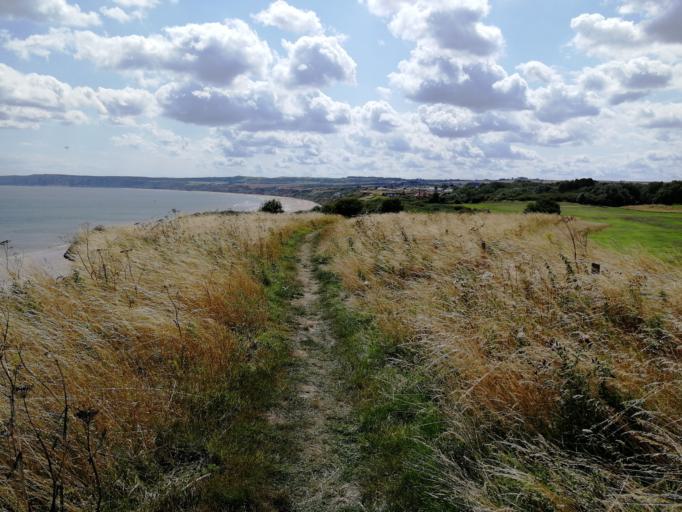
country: GB
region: England
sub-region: North Yorkshire
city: Filey
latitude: 54.1982
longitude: -0.2854
